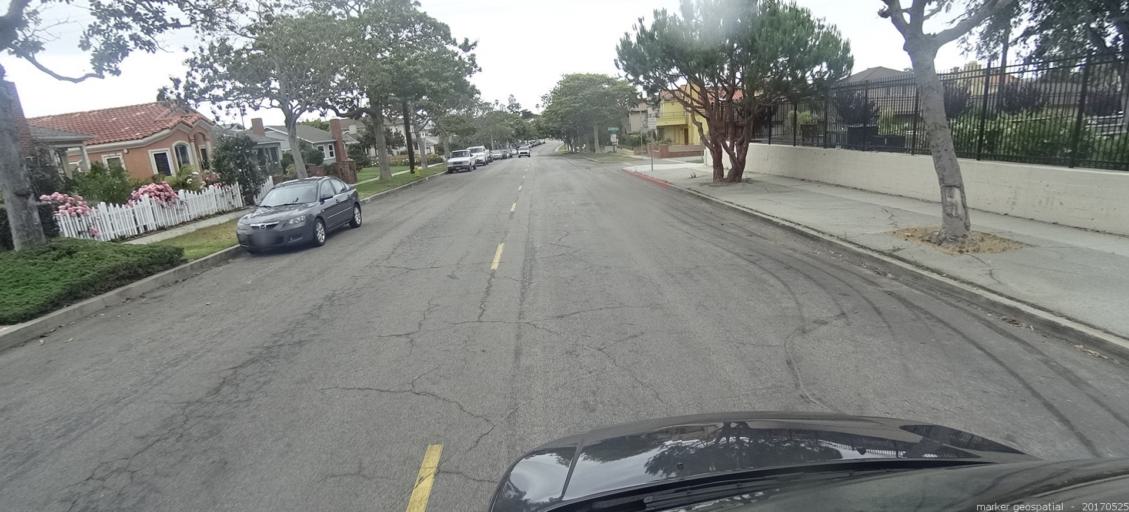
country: US
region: California
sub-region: Los Angeles County
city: Redondo Beach
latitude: 33.8519
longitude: -118.3826
